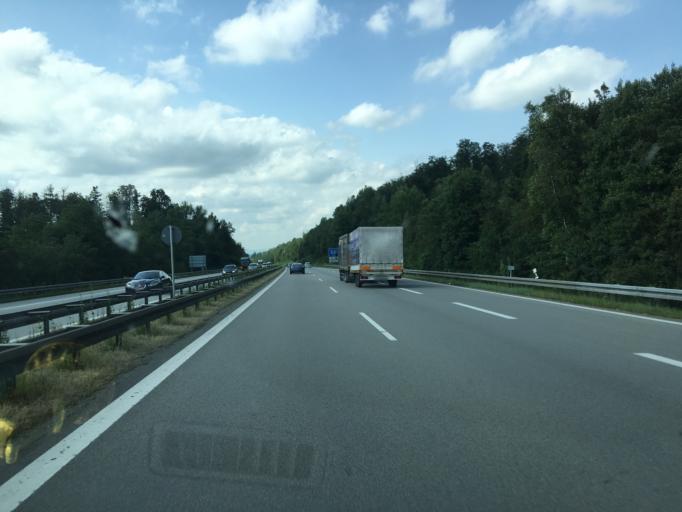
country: DE
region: Bavaria
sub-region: Lower Bavaria
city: Passau
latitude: 48.5478
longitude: 13.3970
